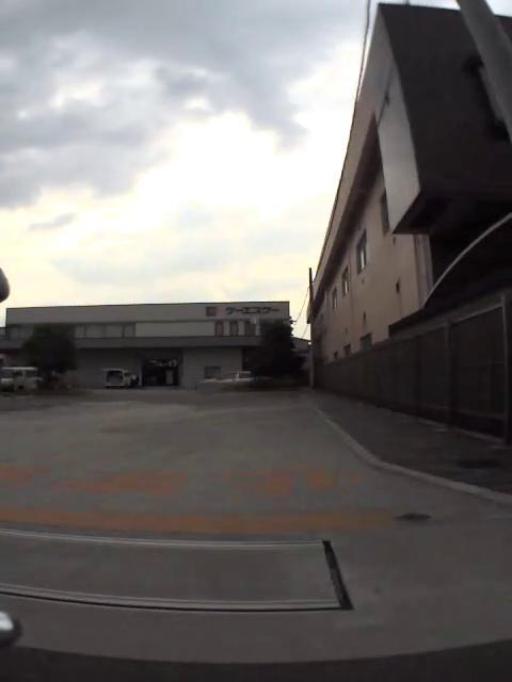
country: JP
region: Osaka
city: Hirakata
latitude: 34.8077
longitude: 135.6326
